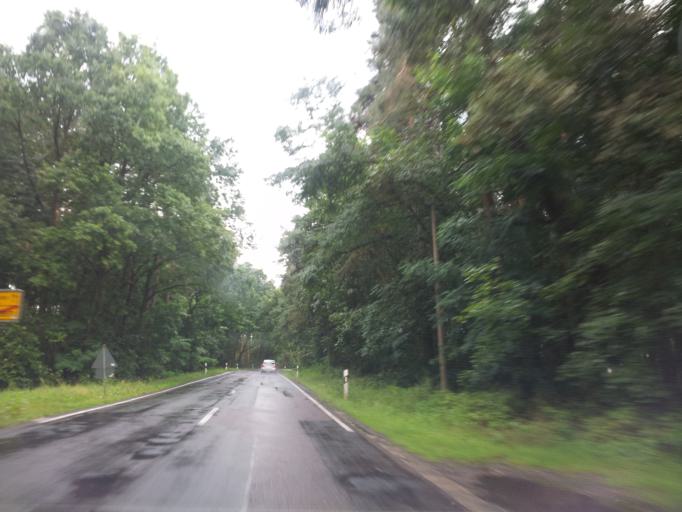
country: DE
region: Brandenburg
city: Graben
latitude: 52.2277
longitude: 12.4238
